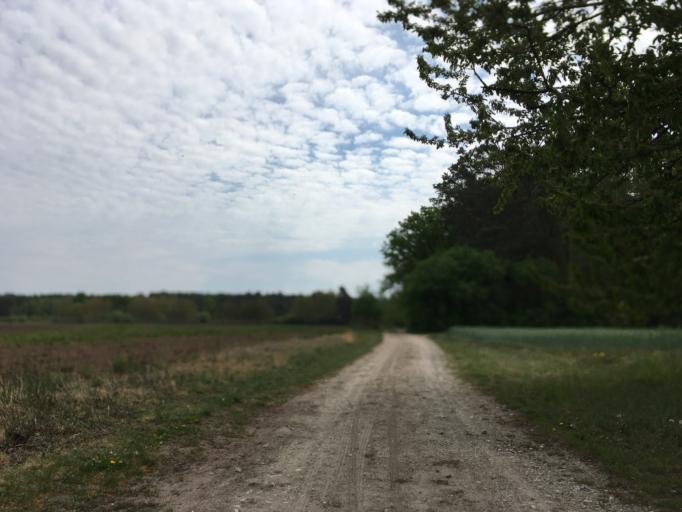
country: DE
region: Brandenburg
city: Rudnitz
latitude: 52.7124
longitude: 13.6251
